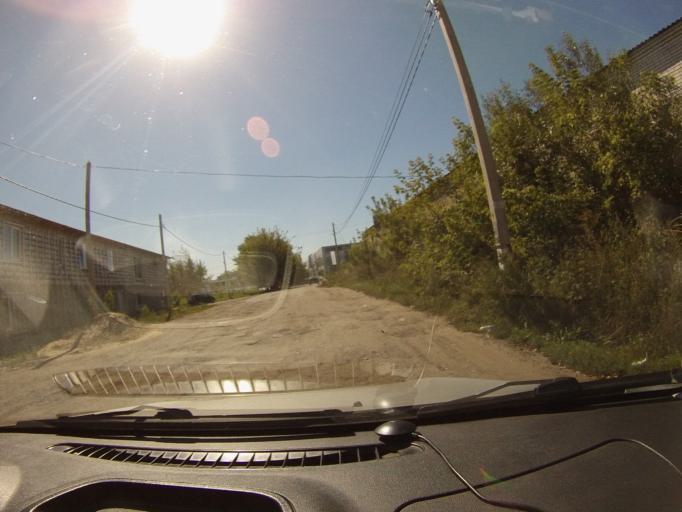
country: RU
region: Tambov
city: Donskoye
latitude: 52.7589
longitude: 41.4658
